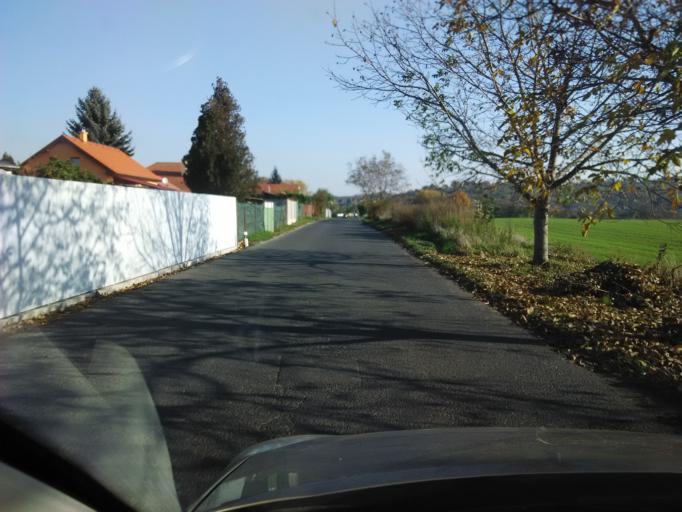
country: SK
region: Nitriansky
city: Levice
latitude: 48.2054
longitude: 18.6161
